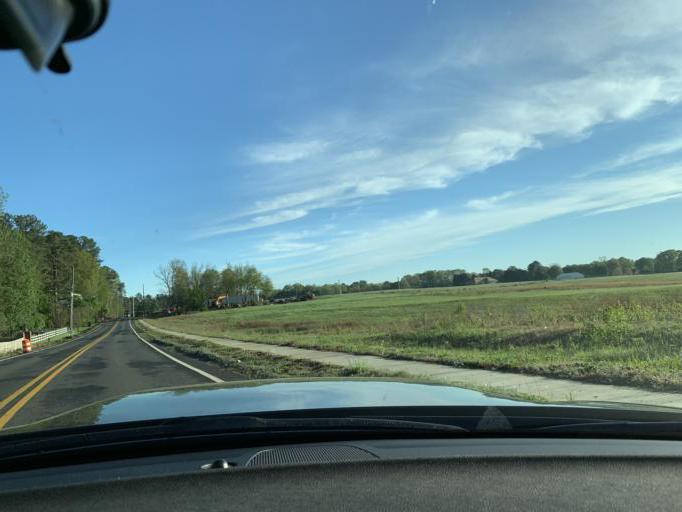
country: US
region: Georgia
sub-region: Fulton County
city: Roswell
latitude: 34.0653
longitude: -84.3742
